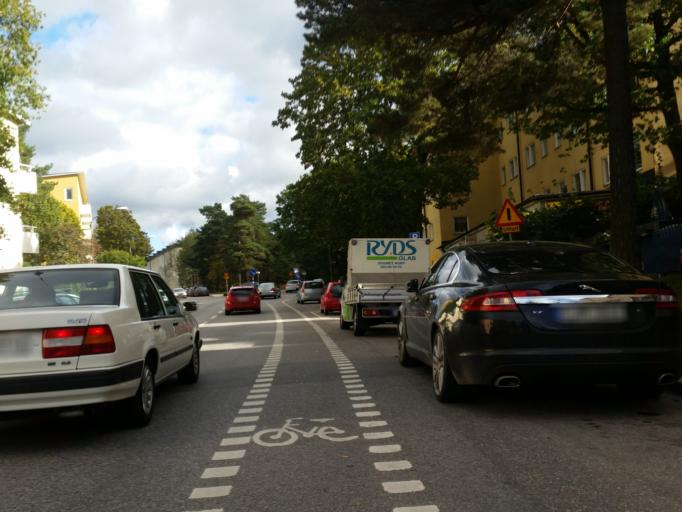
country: SE
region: Stockholm
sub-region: Stockholms Kommun
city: Arsta
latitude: 59.2969
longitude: 18.0930
